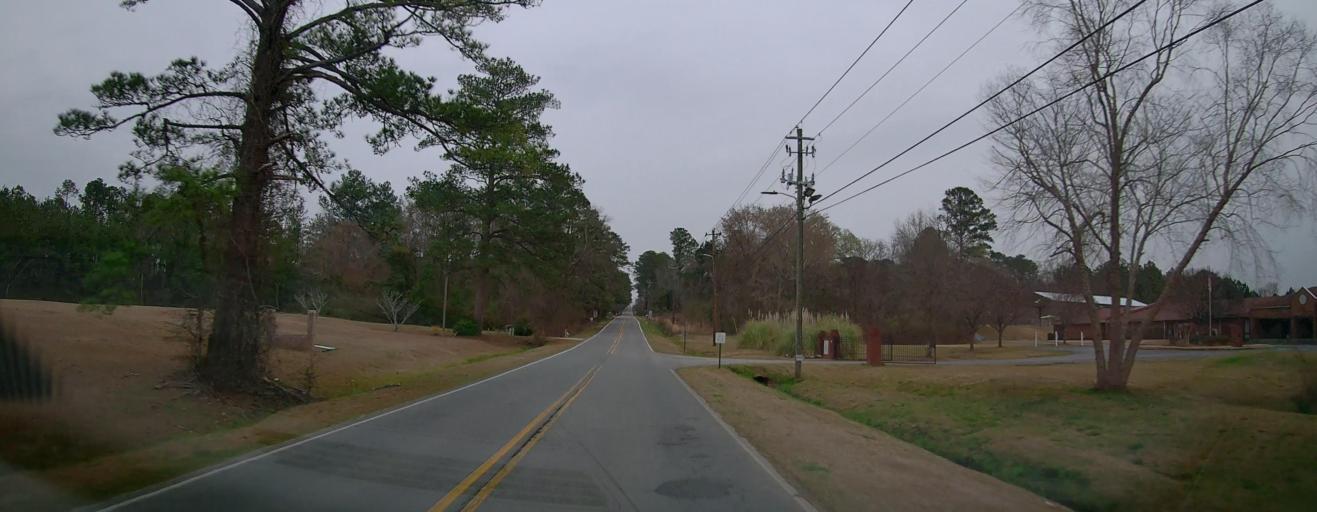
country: US
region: Georgia
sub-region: Bibb County
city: Macon
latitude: 32.8592
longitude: -83.7054
